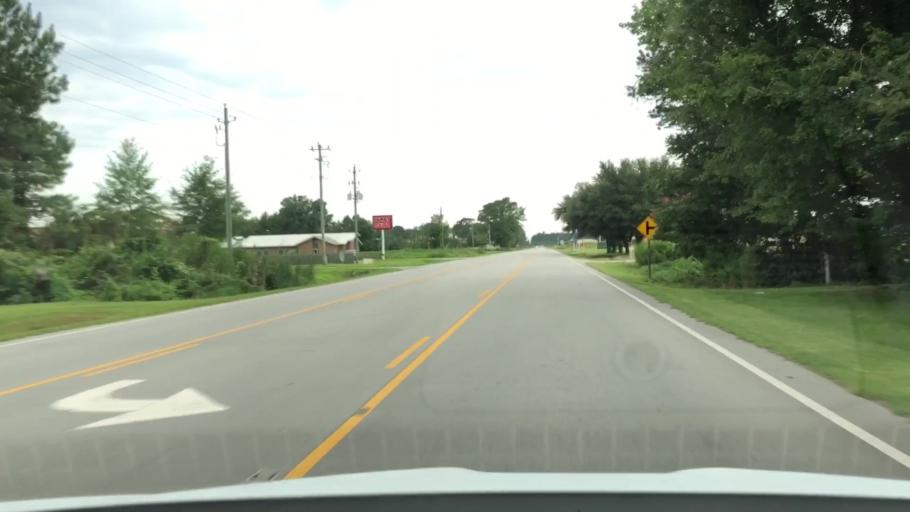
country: US
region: North Carolina
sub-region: Jones County
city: Trenton
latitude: 35.0672
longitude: -77.3643
